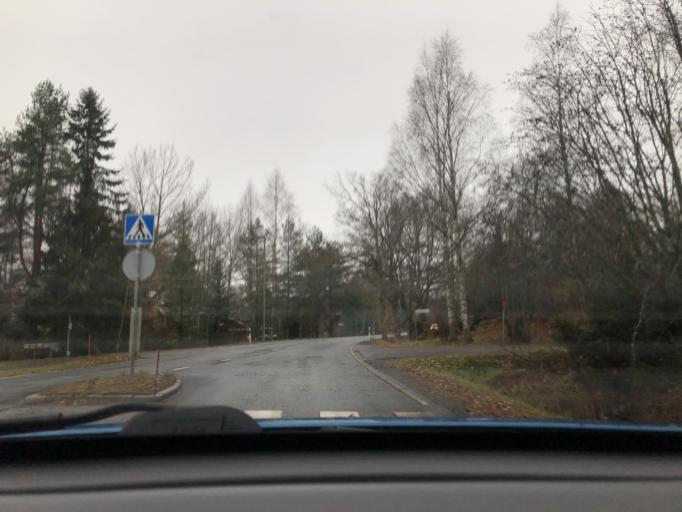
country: FI
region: Pirkanmaa
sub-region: Tampere
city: Kangasala
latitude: 61.4527
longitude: 24.0329
